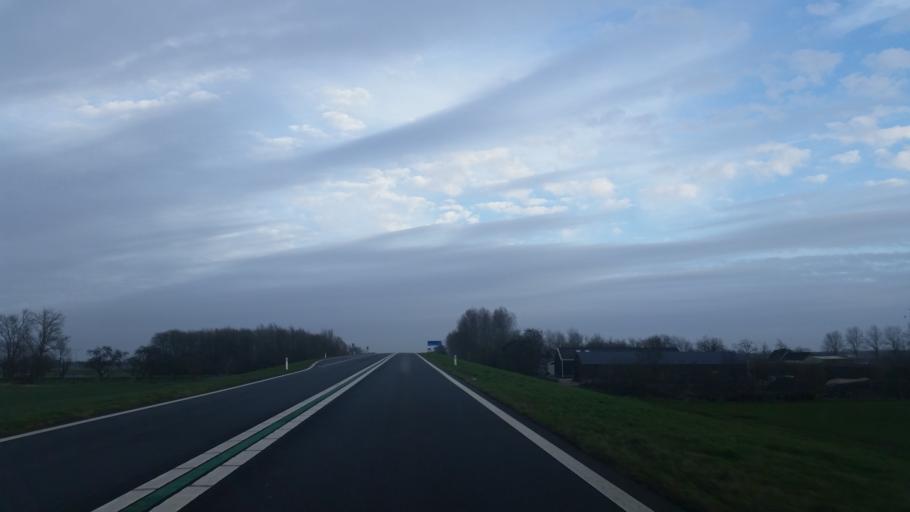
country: NL
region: North Holland
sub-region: Gemeente Beemster
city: Halfweg
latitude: 52.5410
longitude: 4.9040
